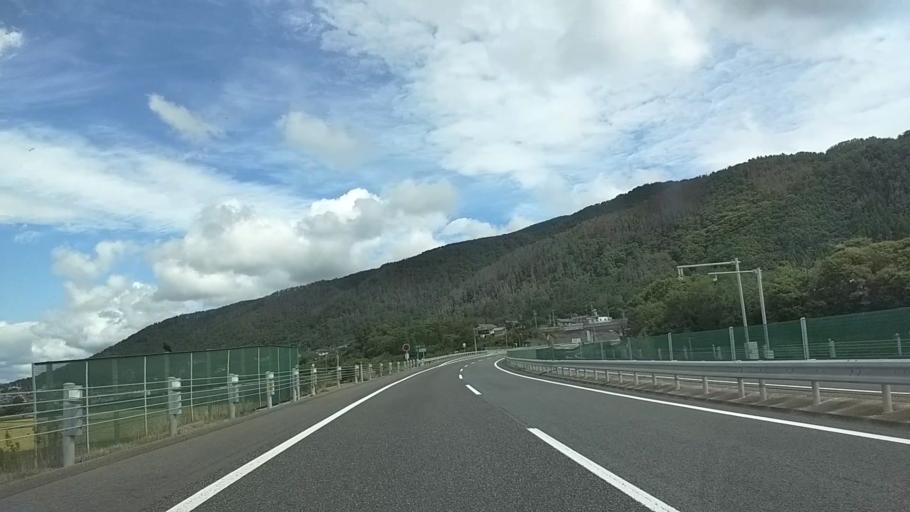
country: JP
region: Nagano
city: Toyoshina
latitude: 36.3257
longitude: 137.9242
